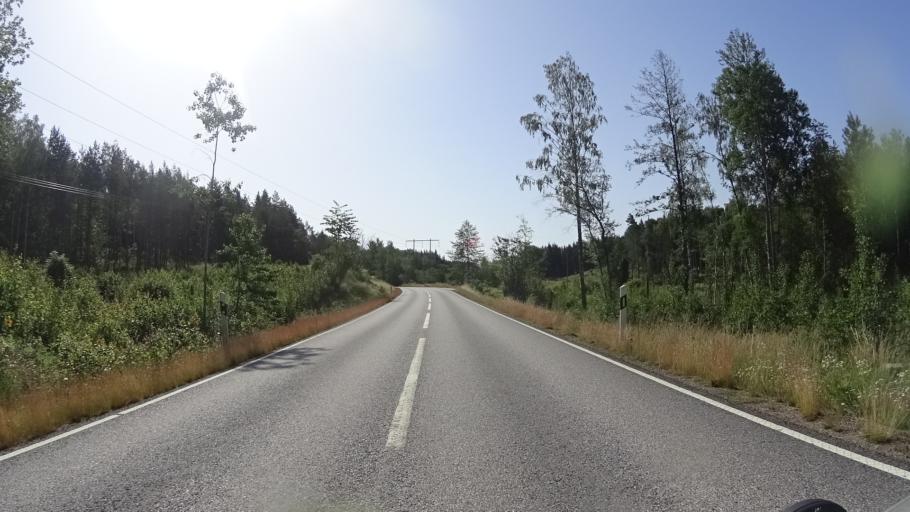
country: SE
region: Kalmar
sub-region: Vasterviks Kommun
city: Overum
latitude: 58.0455
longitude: 16.2135
